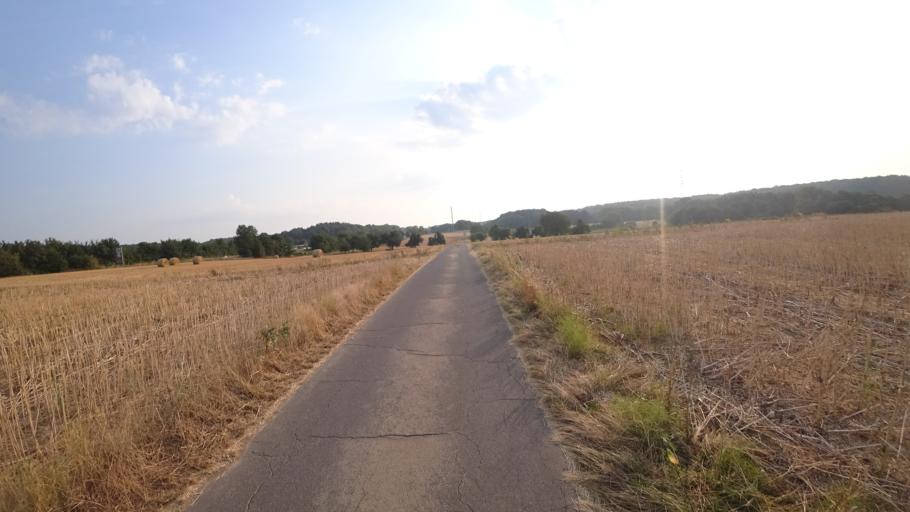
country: DE
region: Rheinland-Pfalz
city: Weitersburg
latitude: 50.4239
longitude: 7.6201
